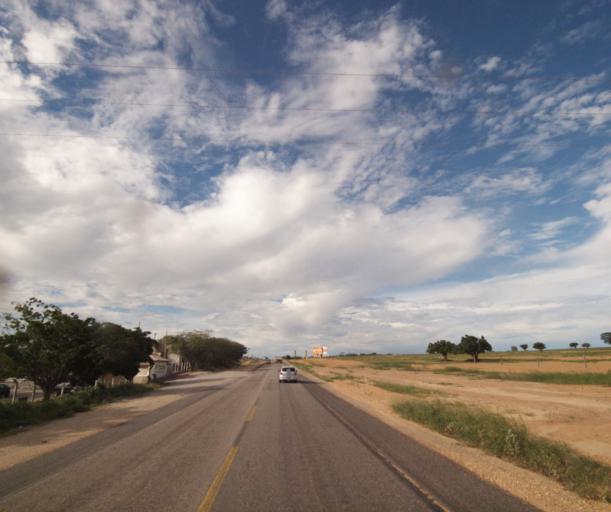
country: BR
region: Bahia
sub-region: Guanambi
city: Guanambi
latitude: -14.2703
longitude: -42.7830
